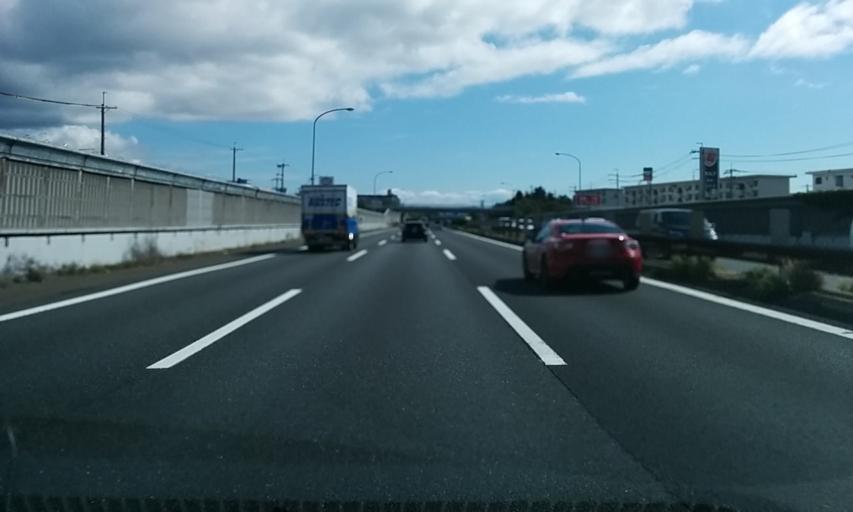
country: JP
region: Hyogo
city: Kawanishi
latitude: 34.8108
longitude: 135.3964
